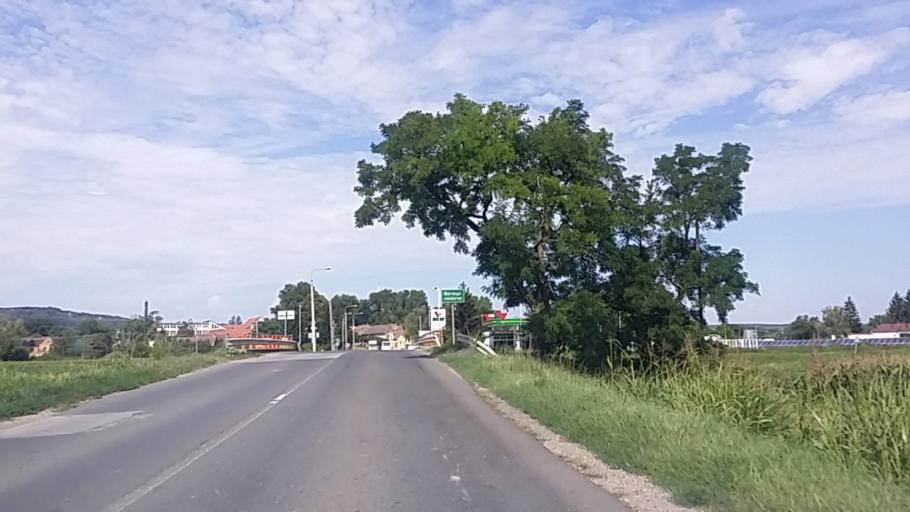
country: HU
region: Baranya
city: Sasd
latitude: 46.2508
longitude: 18.1172
